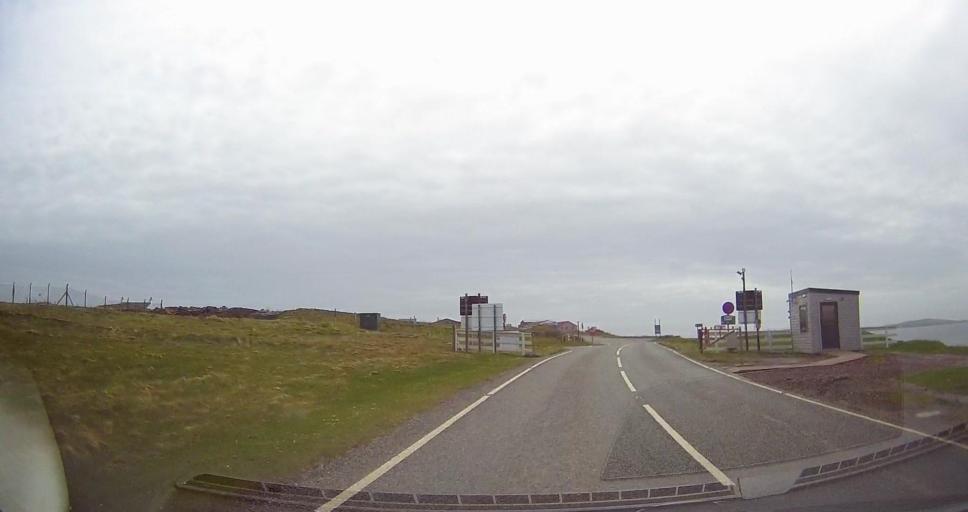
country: GB
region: Scotland
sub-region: Shetland Islands
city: Sandwick
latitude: 59.8802
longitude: -1.3060
